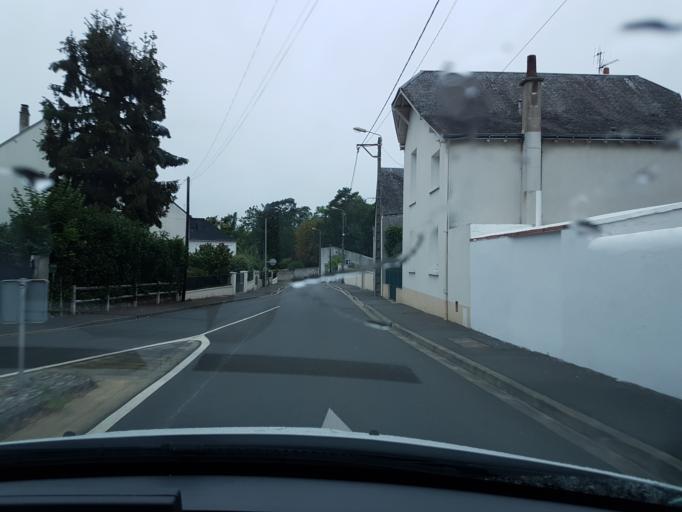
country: FR
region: Centre
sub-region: Departement d'Indre-et-Loire
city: Saint-Avertin
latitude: 47.3668
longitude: 0.7448
